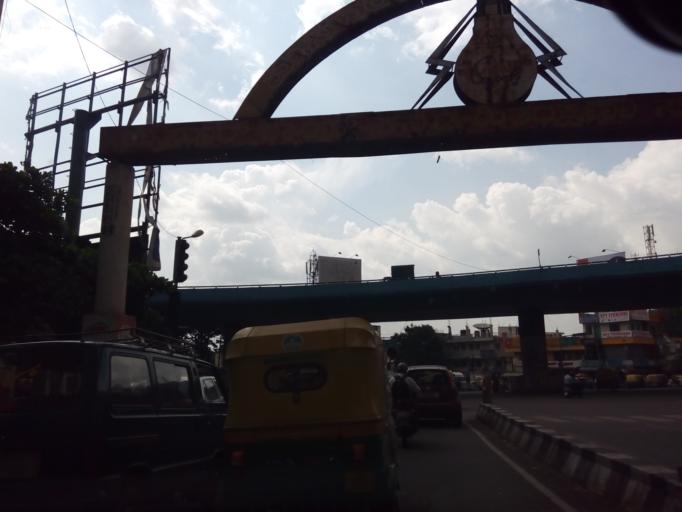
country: IN
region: Karnataka
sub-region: Bangalore Urban
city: Bangalore
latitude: 13.0181
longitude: 77.5578
